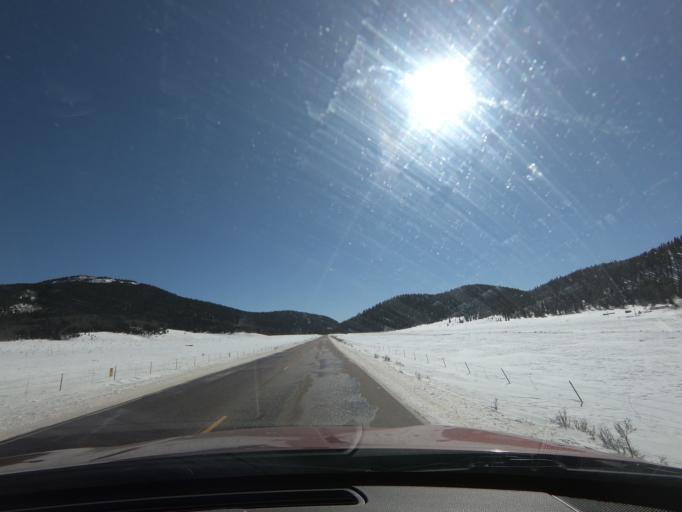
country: US
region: Colorado
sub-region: Teller County
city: Cripple Creek
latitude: 38.7616
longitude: -105.1128
